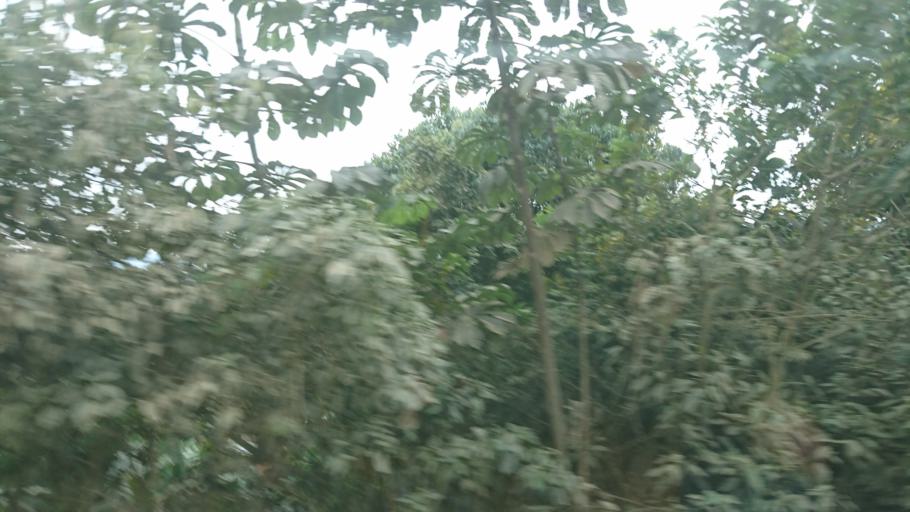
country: BO
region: La Paz
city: Coroico
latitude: -16.2228
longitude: -67.6783
